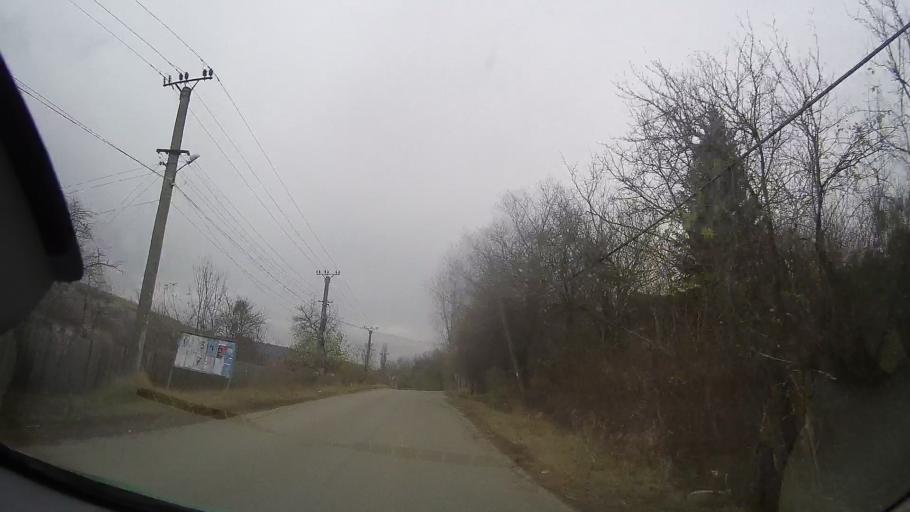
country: RO
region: Prahova
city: Ceptura de Sus
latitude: 45.0518
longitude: 26.2967
